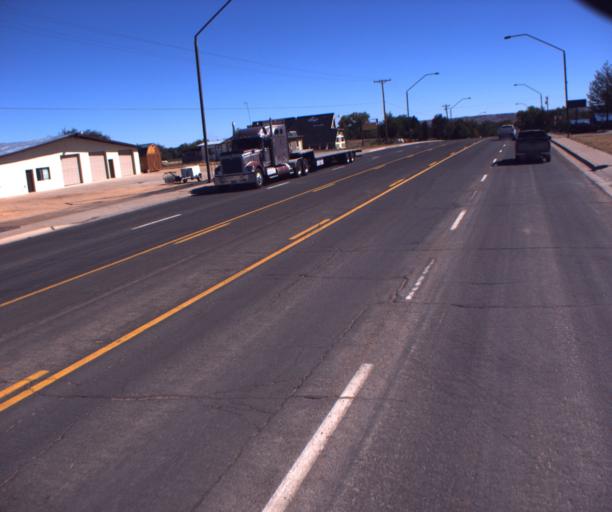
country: US
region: Arizona
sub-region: Apache County
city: Saint Johns
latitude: 34.5065
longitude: -109.3792
